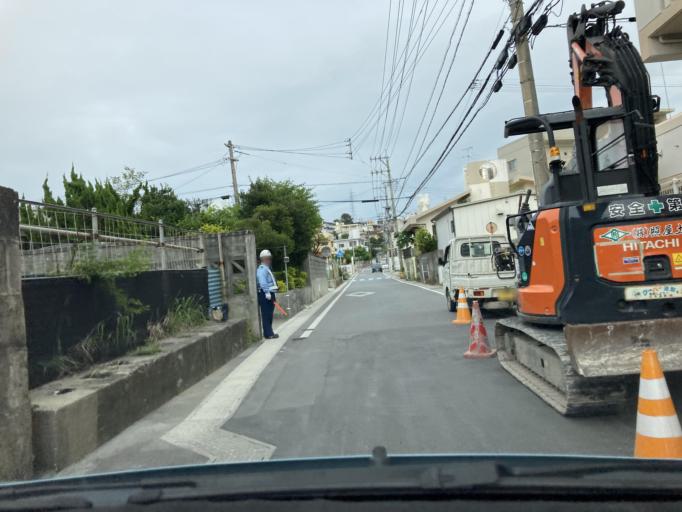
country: JP
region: Okinawa
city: Itoman
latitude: 26.1442
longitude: 127.6740
